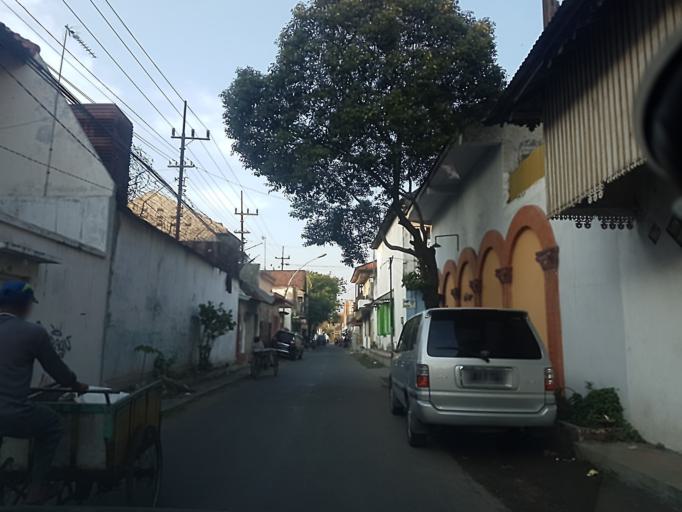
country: ID
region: East Java
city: Gresik
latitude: -7.1586
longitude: 112.6582
